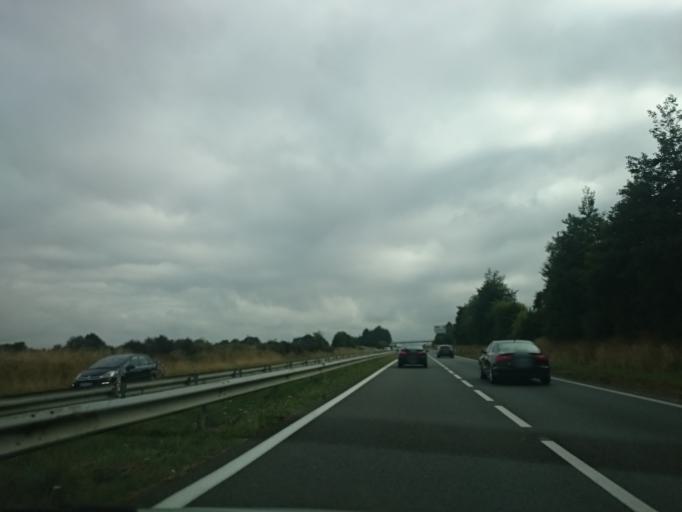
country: FR
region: Brittany
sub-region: Departement des Cotes-d'Armor
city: Tremuson
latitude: 48.5275
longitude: -2.8627
